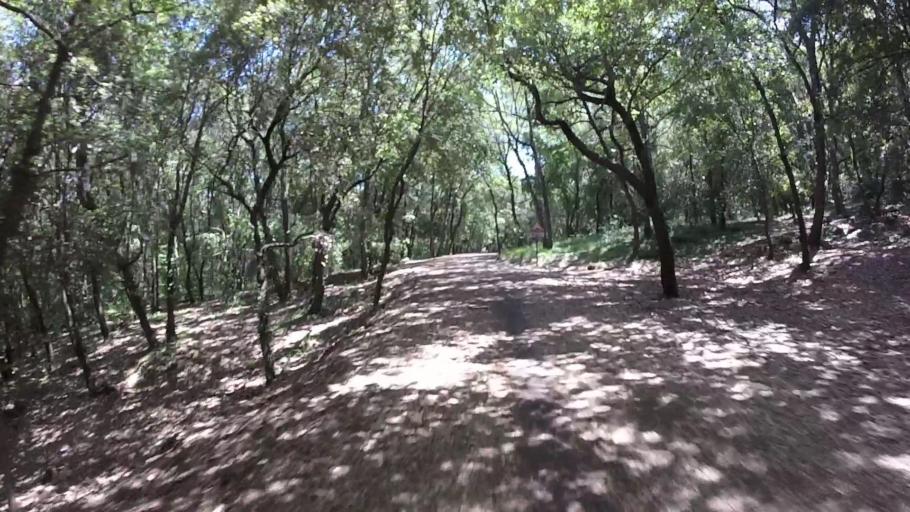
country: FR
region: Provence-Alpes-Cote d'Azur
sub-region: Departement des Alpes-Maritimes
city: Mougins
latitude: 43.6064
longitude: 7.0329
